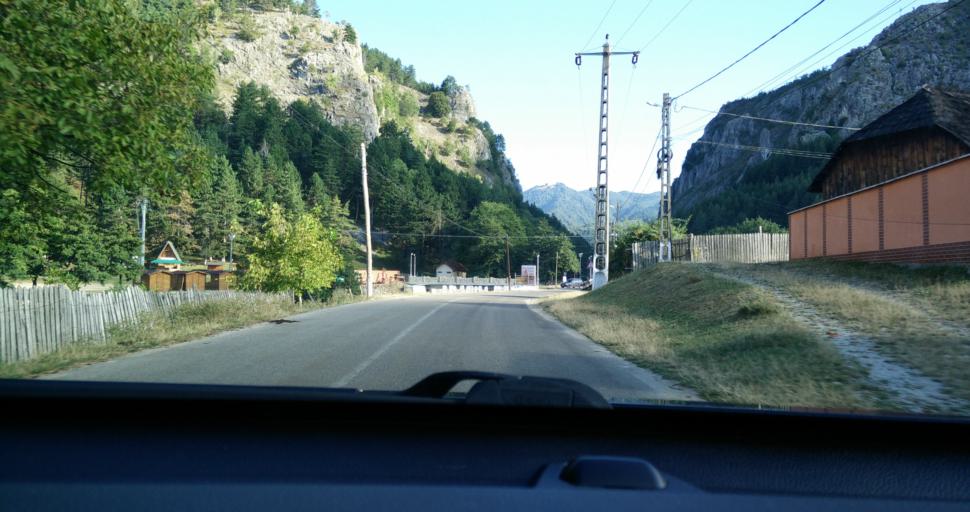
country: RO
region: Gorj
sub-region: Comuna Baia de Fier
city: Baia de Fier
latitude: 45.1851
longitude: 23.7574
